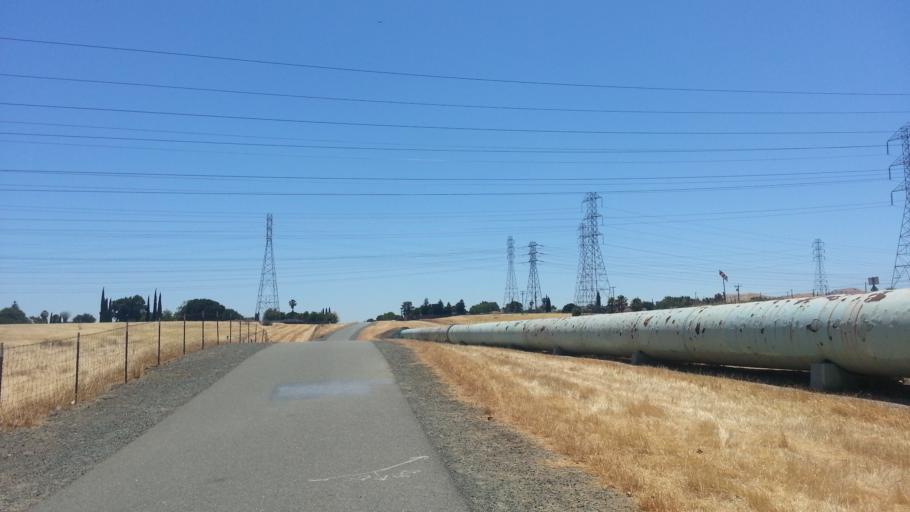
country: US
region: California
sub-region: Contra Costa County
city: Pittsburg
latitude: 38.0146
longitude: -121.9100
